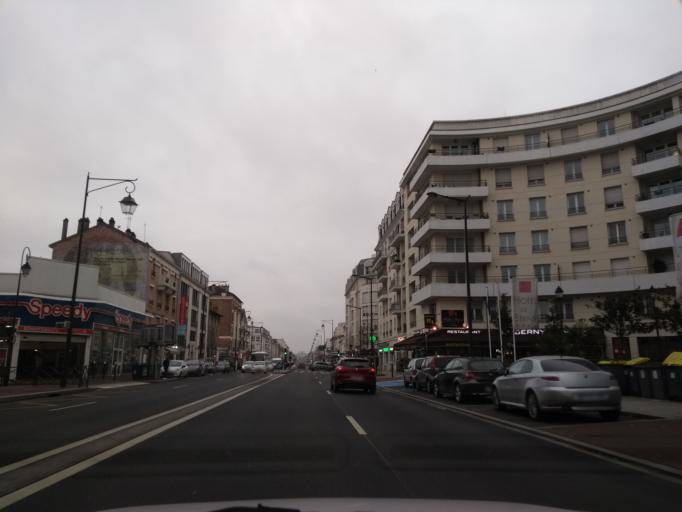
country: FR
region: Ile-de-France
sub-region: Departement des Hauts-de-Seine
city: Antony
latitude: 48.7627
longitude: 2.3086
